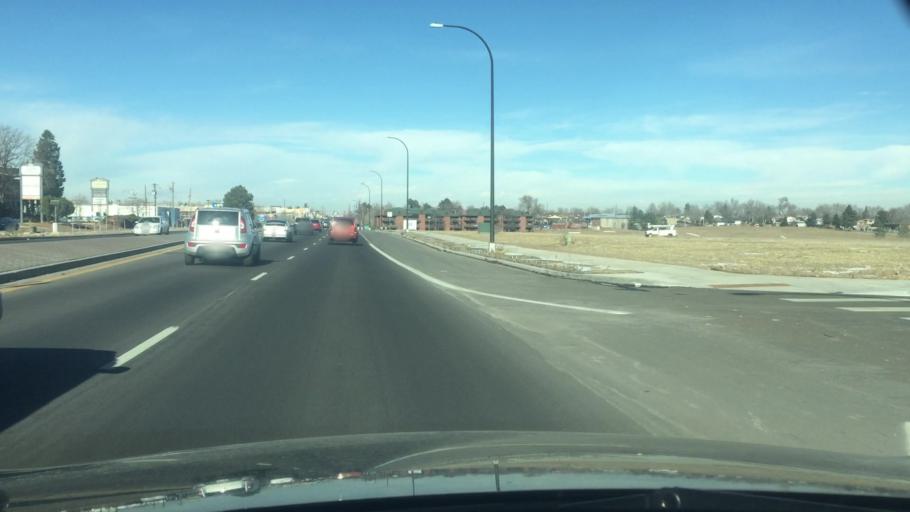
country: US
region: Colorado
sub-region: Jefferson County
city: Lakewood
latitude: 39.6772
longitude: -105.0814
